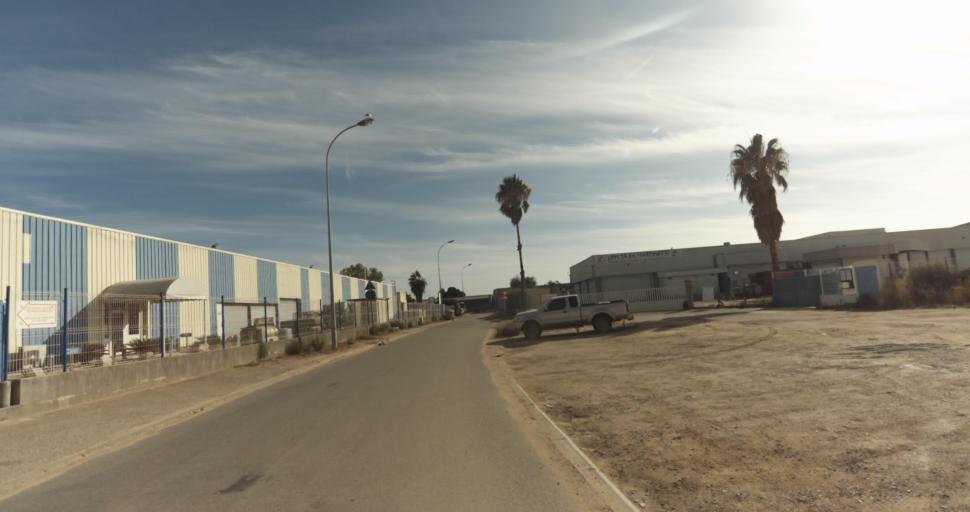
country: FR
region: Corsica
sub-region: Departement de la Corse-du-Sud
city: Afa
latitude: 41.9306
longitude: 8.7899
